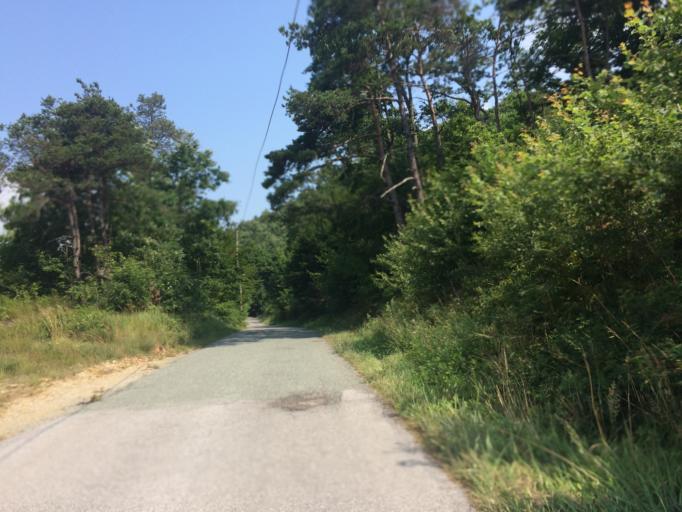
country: IT
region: Liguria
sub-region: Provincia di Savona
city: Molino-Pera
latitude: 44.4824
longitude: 8.3525
